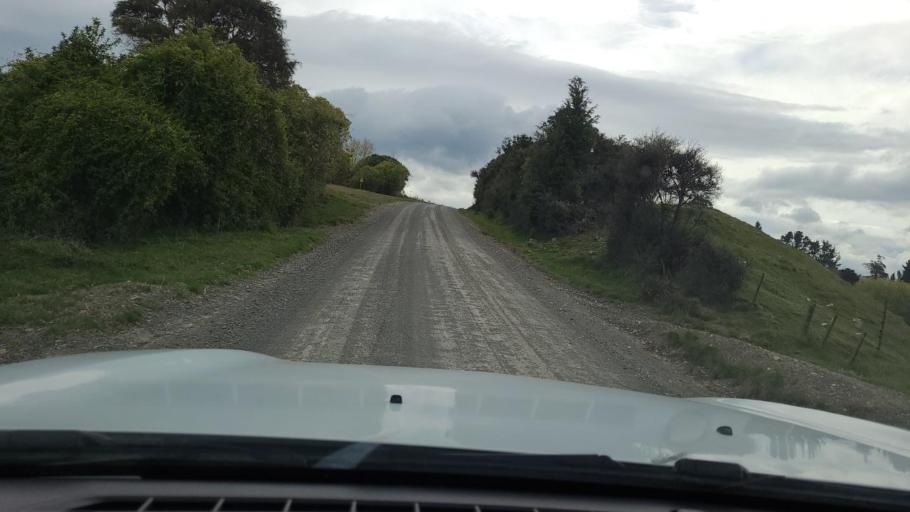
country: NZ
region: Hawke's Bay
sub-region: Napier City
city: Napier
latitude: -39.3180
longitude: 176.8387
